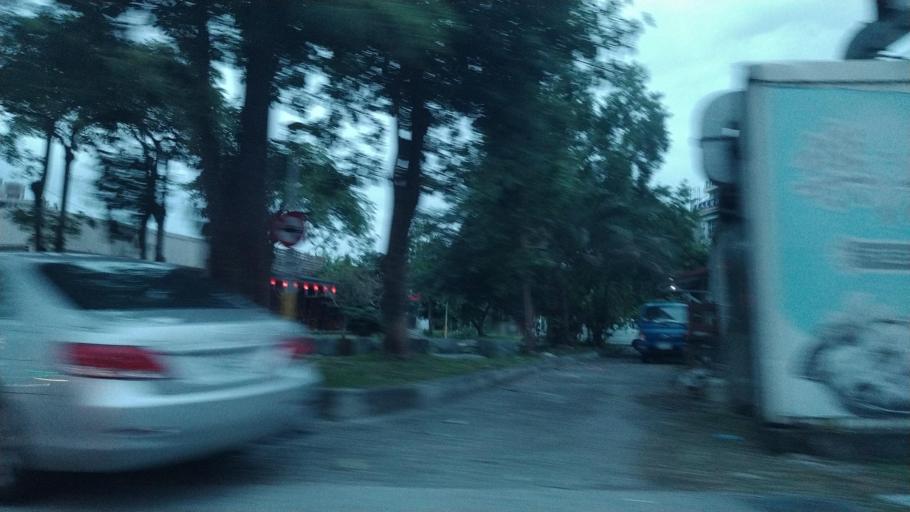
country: TW
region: Taiwan
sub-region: Hualien
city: Hualian
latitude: 23.9773
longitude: 121.6009
